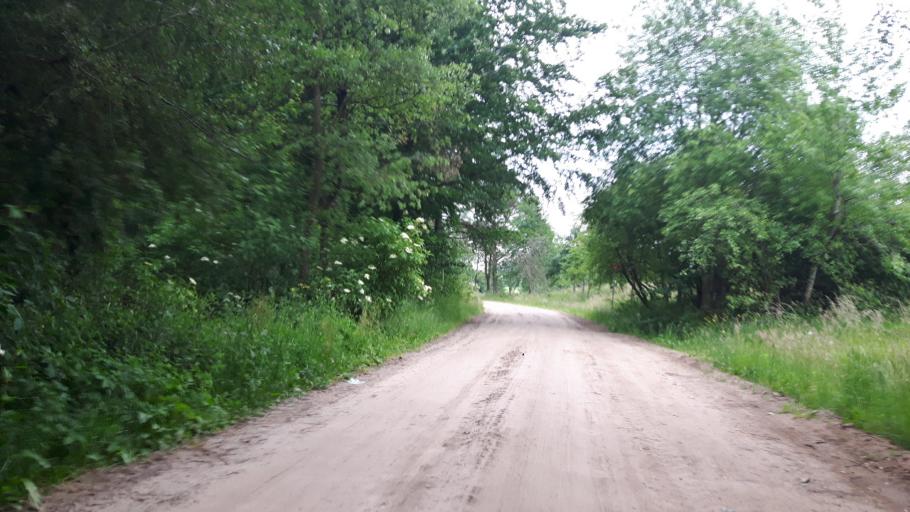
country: PL
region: Warmian-Masurian Voivodeship
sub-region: Powiat elblaski
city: Tolkmicko
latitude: 54.3193
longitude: 19.6076
